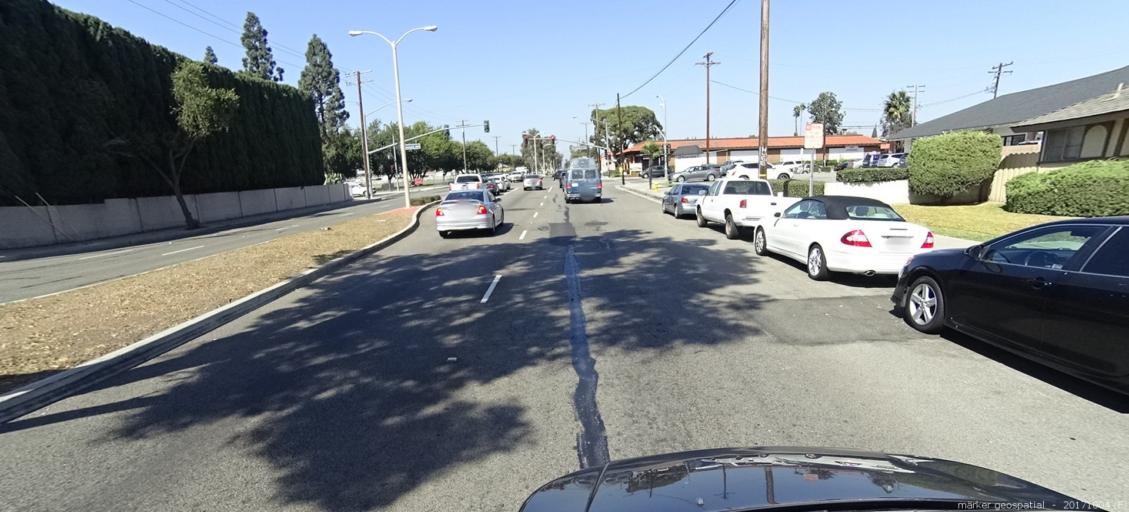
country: US
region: California
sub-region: Orange County
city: Garden Grove
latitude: 33.7952
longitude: -117.9412
